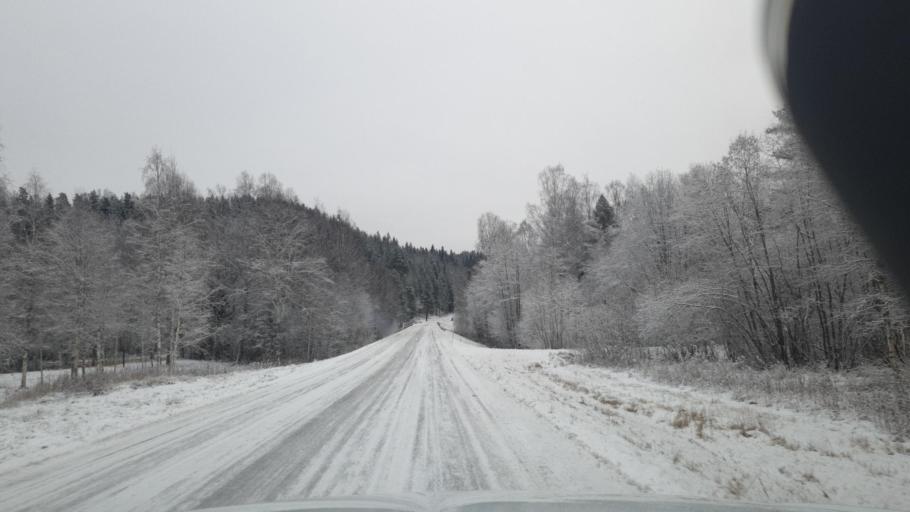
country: NO
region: Ostfold
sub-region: Romskog
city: Romskog
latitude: 59.6988
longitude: 12.0834
